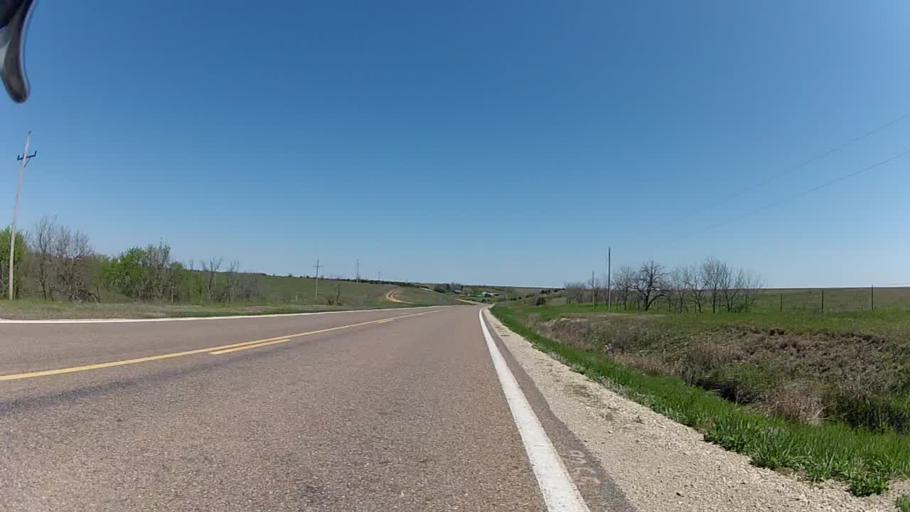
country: US
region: Kansas
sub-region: Wabaunsee County
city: Alma
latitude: 38.9178
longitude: -96.5201
